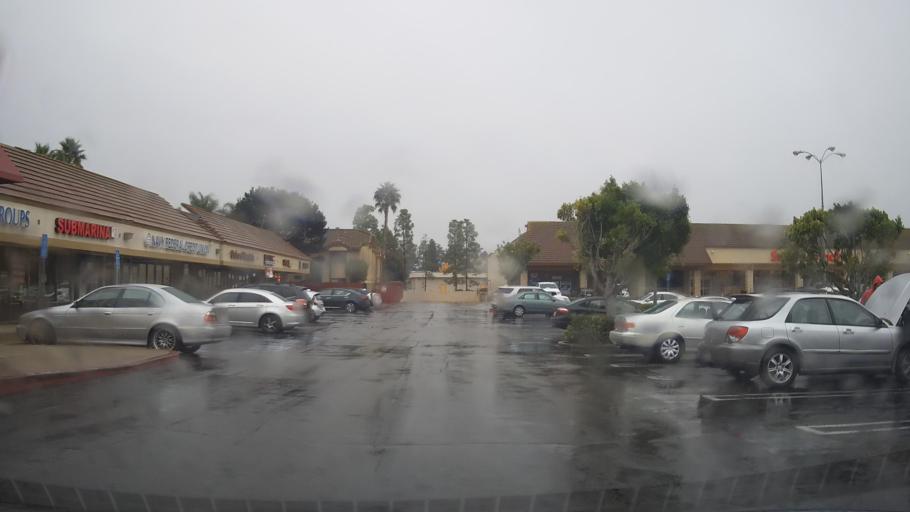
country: US
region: California
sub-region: San Diego County
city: La Mesa
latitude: 32.8219
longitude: -117.1004
